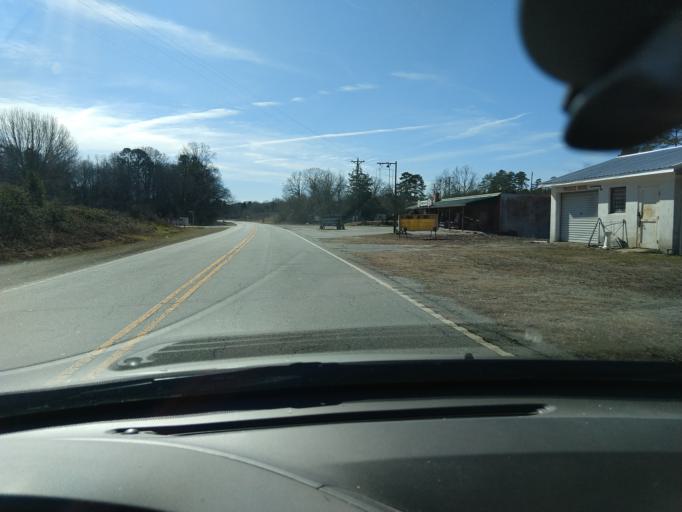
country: US
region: South Carolina
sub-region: Oconee County
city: Westminster
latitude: 34.6567
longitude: -83.1317
